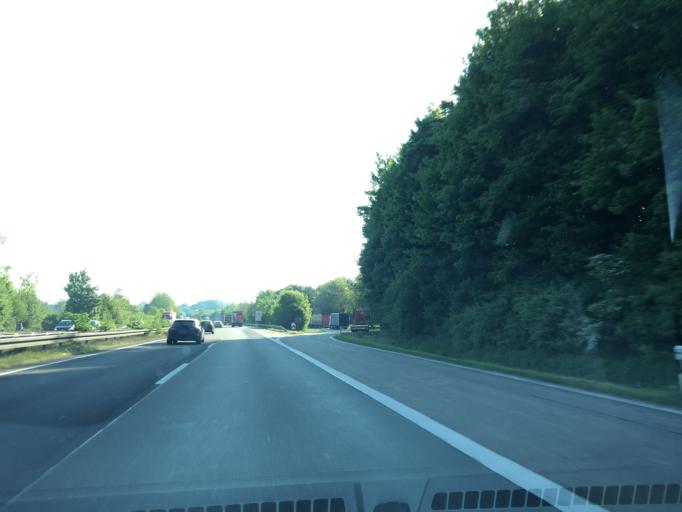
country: DE
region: Lower Saxony
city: Hasbergen
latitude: 52.2434
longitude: 7.8991
